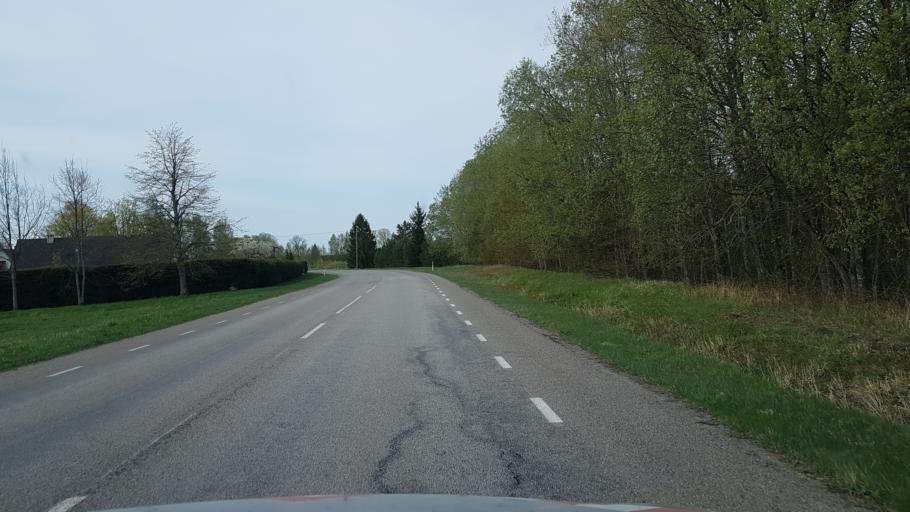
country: EE
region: Paernumaa
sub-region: Audru vald
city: Audru
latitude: 58.3667
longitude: 24.2652
